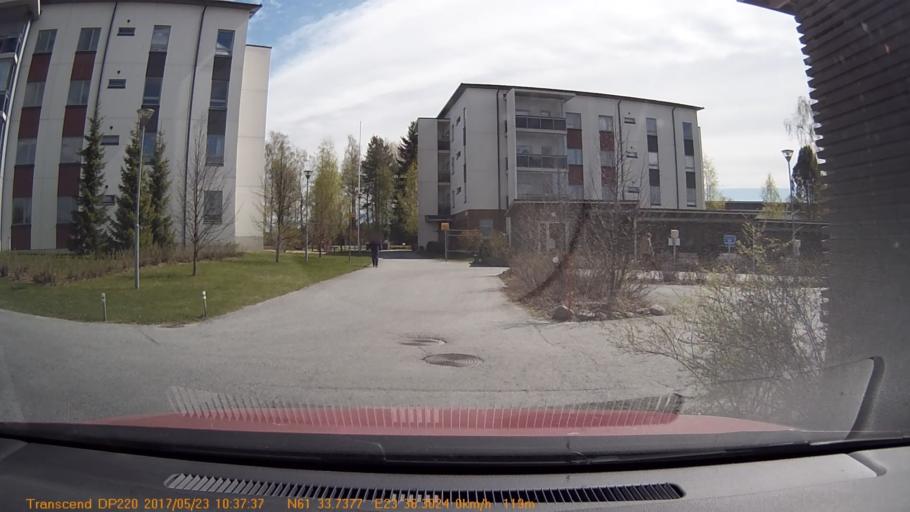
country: FI
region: Pirkanmaa
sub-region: Tampere
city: Yloejaervi
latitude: 61.5623
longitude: 23.6051
